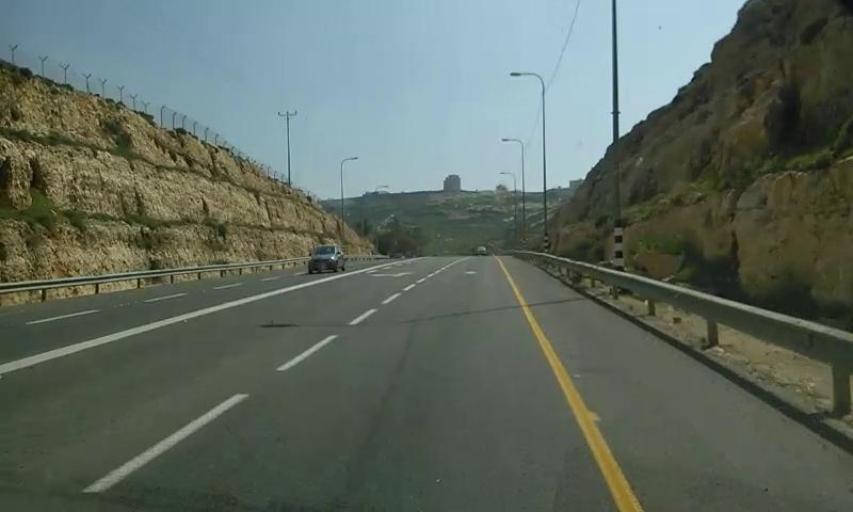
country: PS
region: West Bank
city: Jaba`
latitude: 31.8656
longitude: 35.2591
